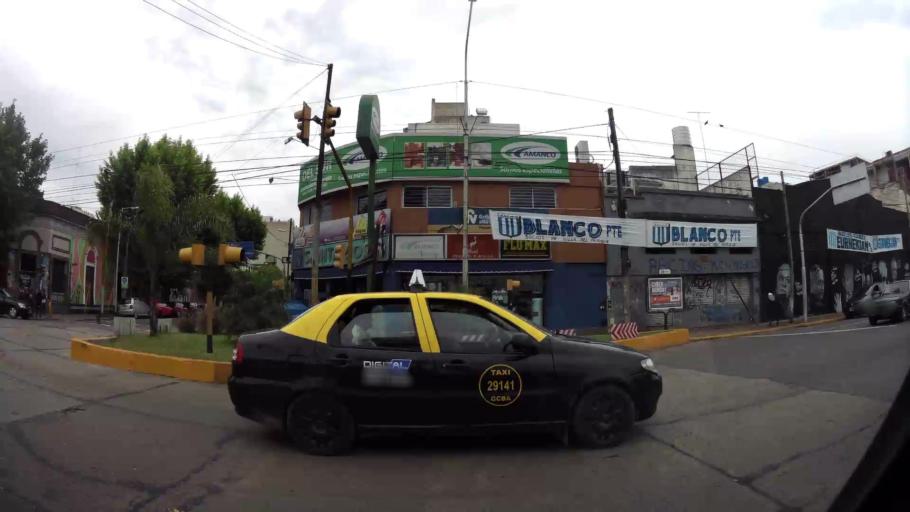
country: AR
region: Buenos Aires
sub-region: Partido de Avellaneda
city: Avellaneda
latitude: -34.6678
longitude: -58.3643
